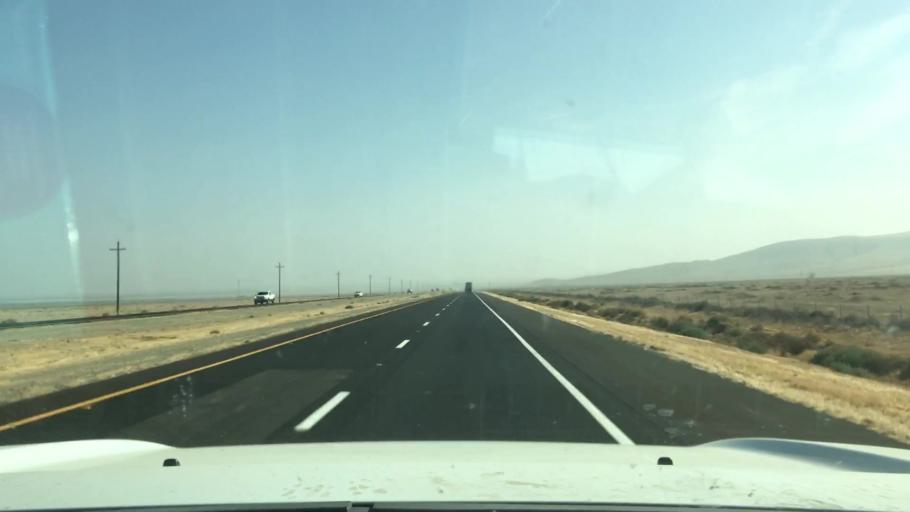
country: US
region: California
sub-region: San Luis Obispo County
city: Shandon
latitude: 35.6652
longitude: -120.0703
